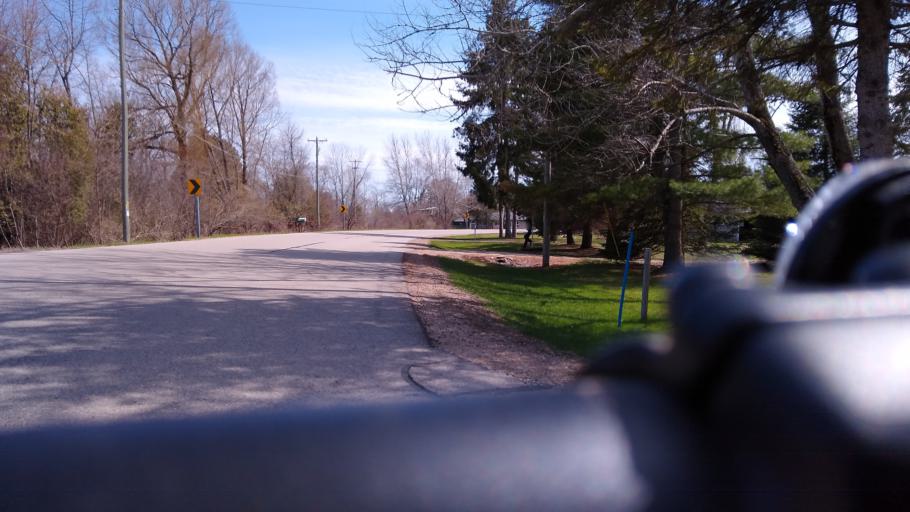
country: US
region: Michigan
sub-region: Delta County
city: Escanaba
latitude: 45.6810
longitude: -87.1444
